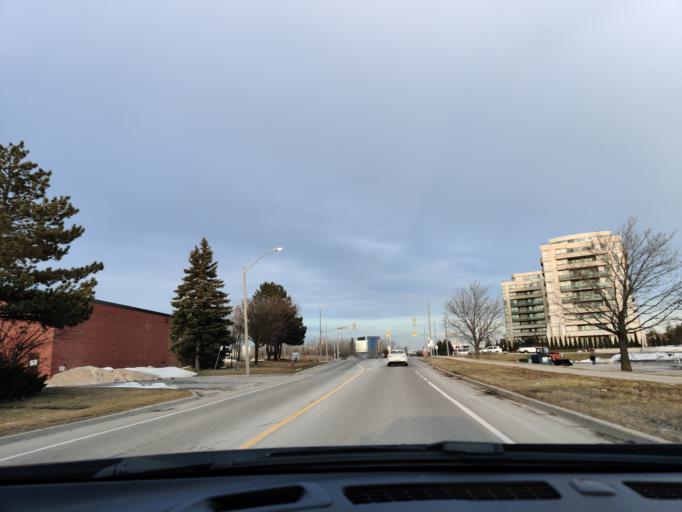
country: CA
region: Ontario
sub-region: York
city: Richmond Hill
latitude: 43.8496
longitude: -79.3785
